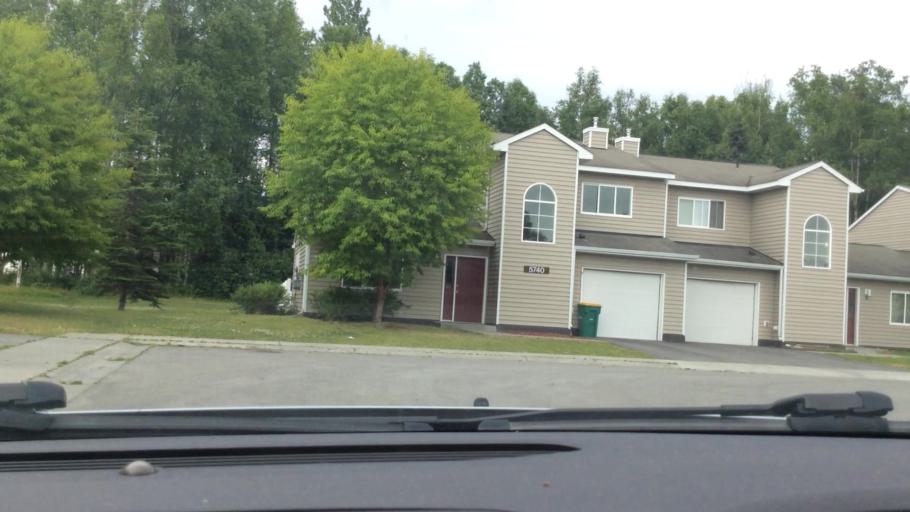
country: US
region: Alaska
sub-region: Anchorage Municipality
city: Anchorage
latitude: 61.2338
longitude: -149.7701
